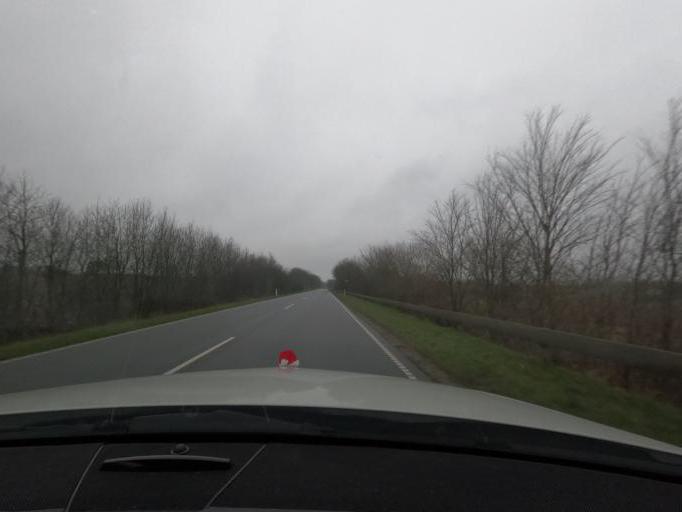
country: DK
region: South Denmark
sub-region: Haderslev Kommune
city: Haderslev
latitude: 55.1841
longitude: 9.4048
